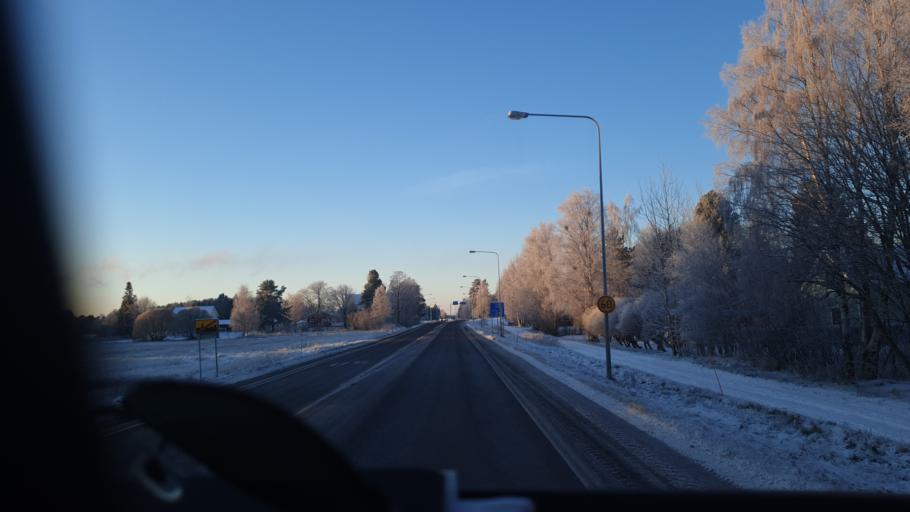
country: FI
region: Northern Ostrobothnia
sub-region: Ylivieska
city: Kalajoki
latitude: 64.2536
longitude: 23.9266
